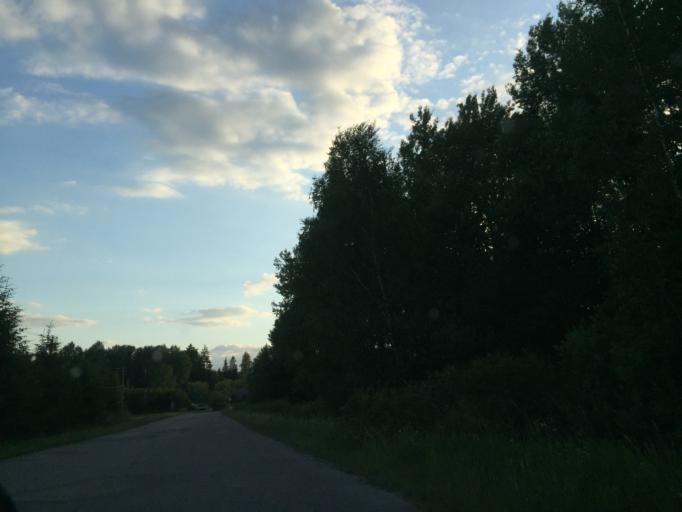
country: LV
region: Sigulda
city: Sigulda
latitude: 57.1081
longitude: 24.9279
